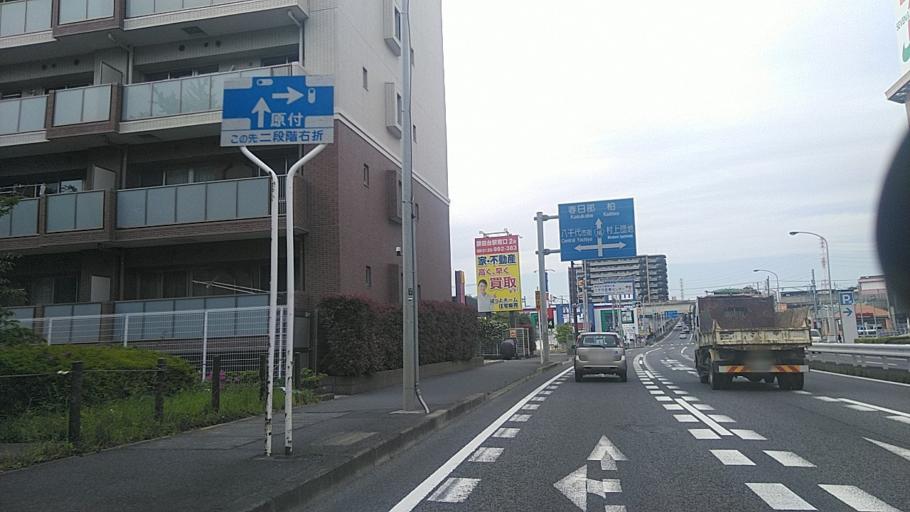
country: JP
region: Chiba
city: Yotsukaido
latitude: 35.7221
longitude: 140.1165
